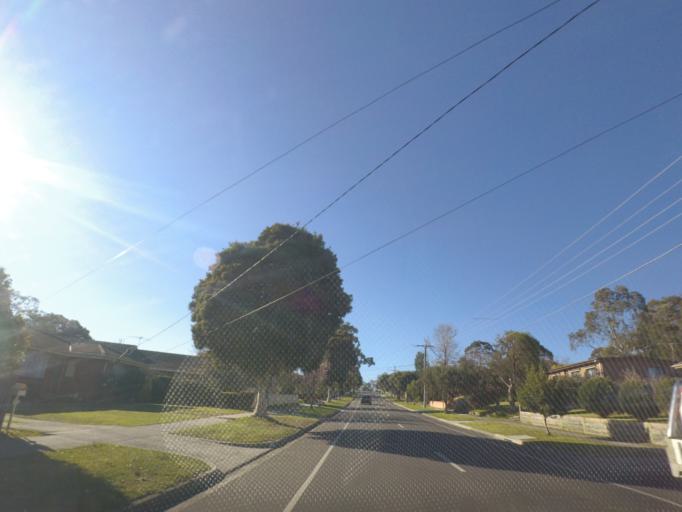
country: AU
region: Victoria
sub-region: Yarra Ranges
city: Kilsyth
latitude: -37.7946
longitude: 145.3137
